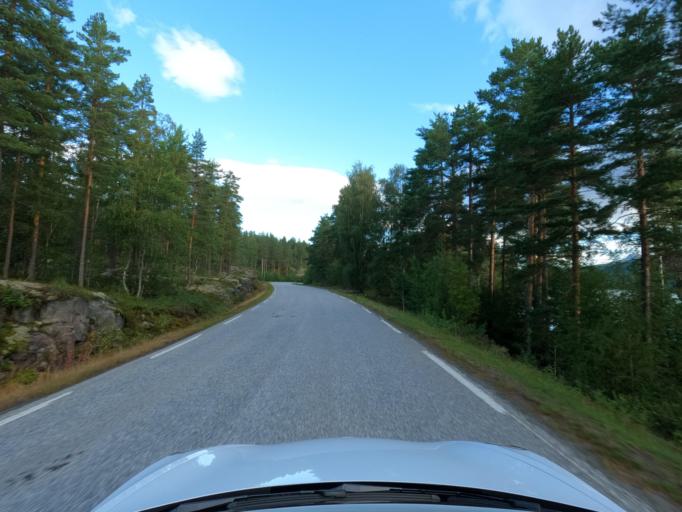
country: NO
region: Telemark
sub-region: Hjartdal
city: Sauland
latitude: 59.7948
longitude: 9.0910
